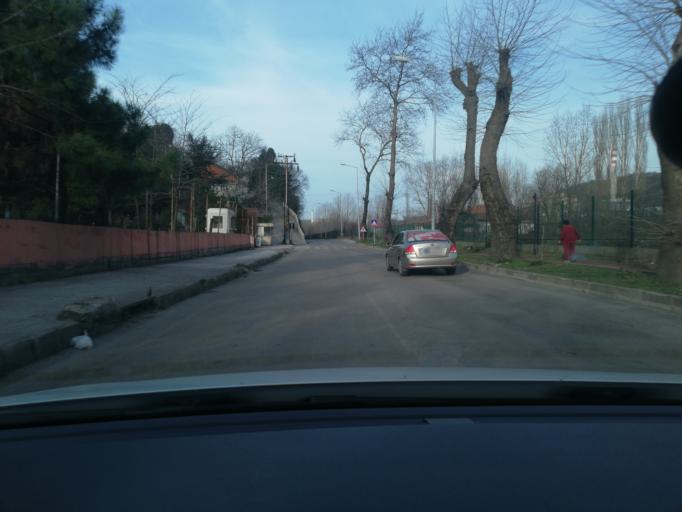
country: TR
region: Zonguldak
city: Kilimli
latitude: 41.5040
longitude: 31.8834
